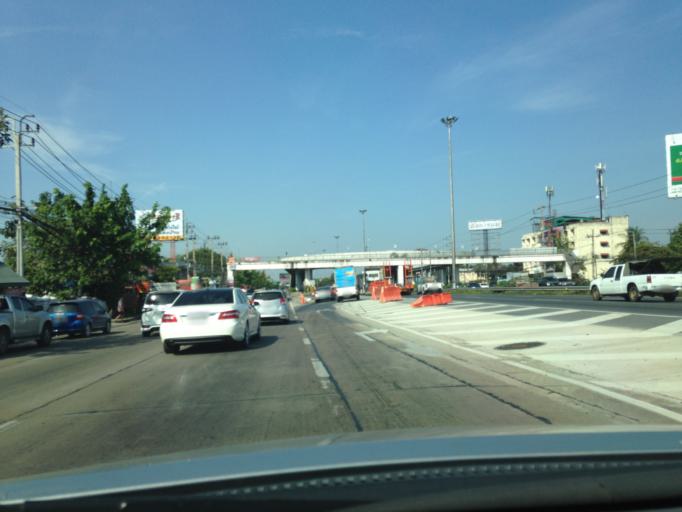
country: TH
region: Nonthaburi
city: Bang Yai
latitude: 13.8290
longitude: 100.4129
